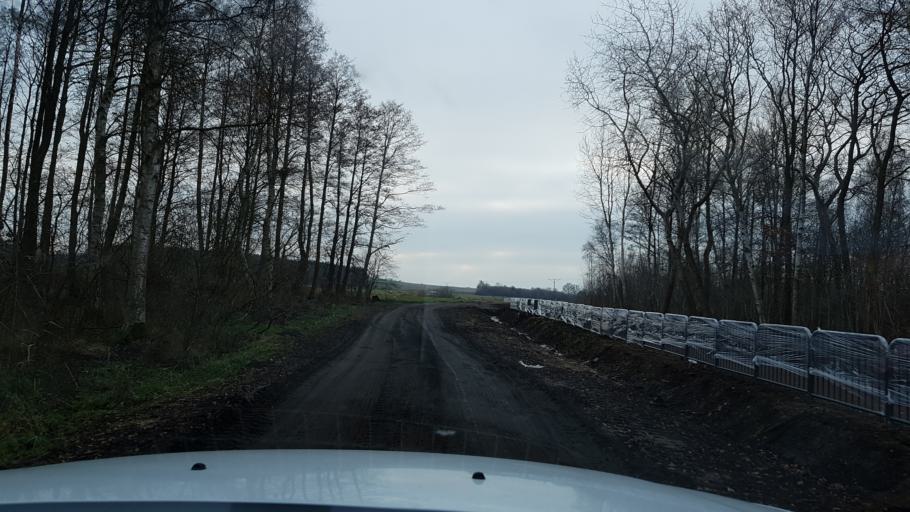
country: PL
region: West Pomeranian Voivodeship
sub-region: Powiat kolobrzeski
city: Grzybowo
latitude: 54.1305
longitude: 15.5158
